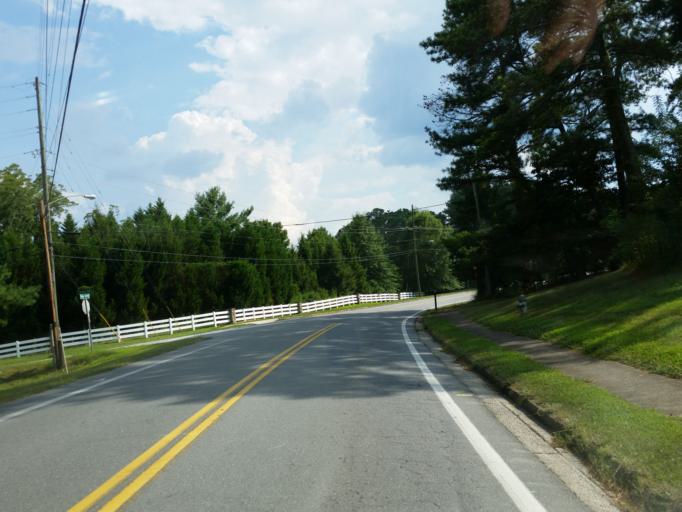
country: US
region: Georgia
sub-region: Fulton County
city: Roswell
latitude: 34.0476
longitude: -84.3960
